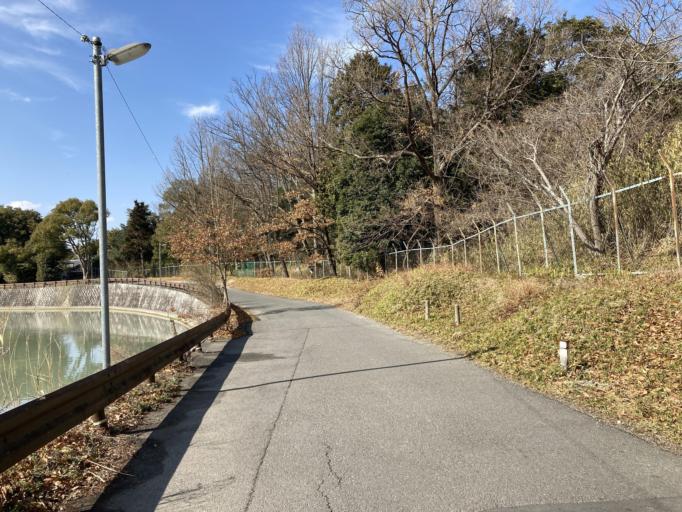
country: JP
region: Nara
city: Nara-shi
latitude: 34.6988
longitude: 135.8056
